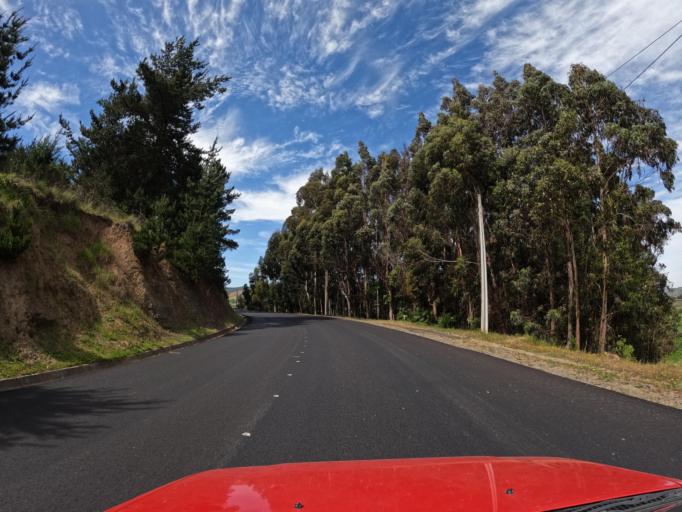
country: CL
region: Maule
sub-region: Provincia de Talca
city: Constitucion
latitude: -35.0786
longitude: -72.0310
